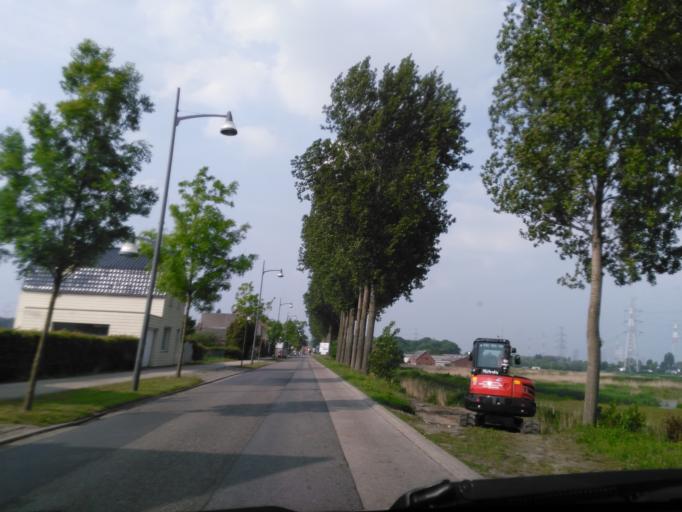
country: BE
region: Flanders
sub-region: Provincie Oost-Vlaanderen
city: Beveren
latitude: 51.2476
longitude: 4.2754
